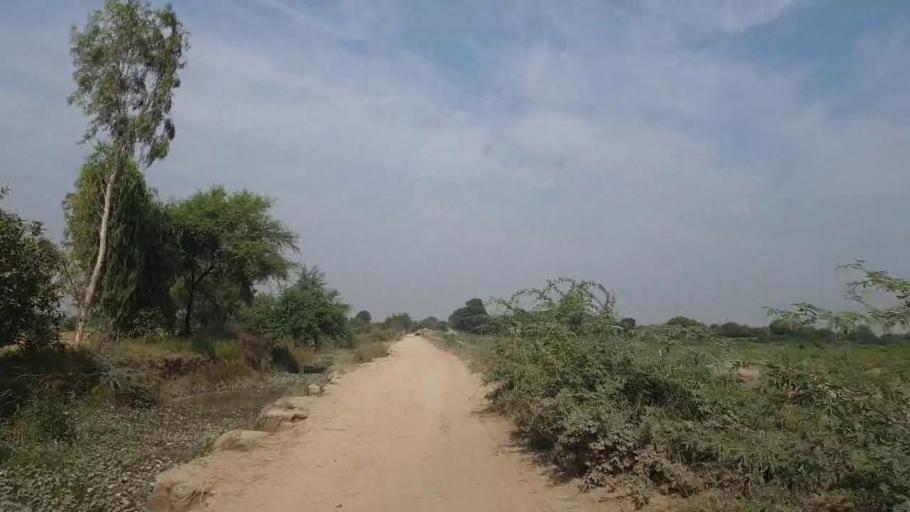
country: PK
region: Sindh
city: Tando Bago
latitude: 24.8906
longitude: 69.0013
